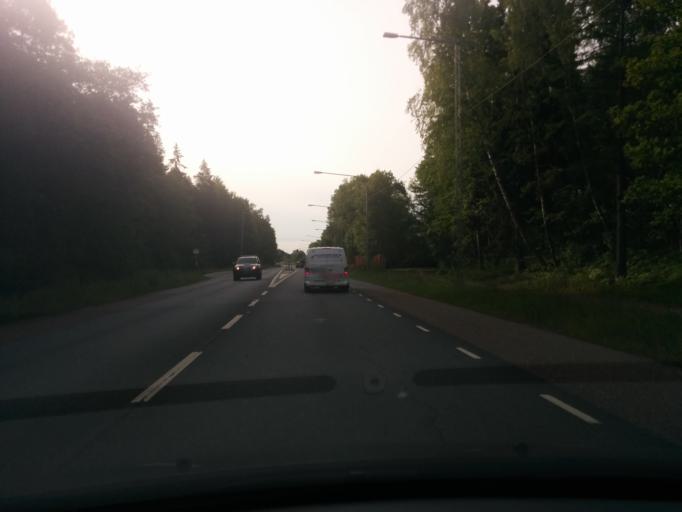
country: SE
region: Stockholm
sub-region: Norrtalje Kommun
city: Bergshamra
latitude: 59.4169
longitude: 18.0115
